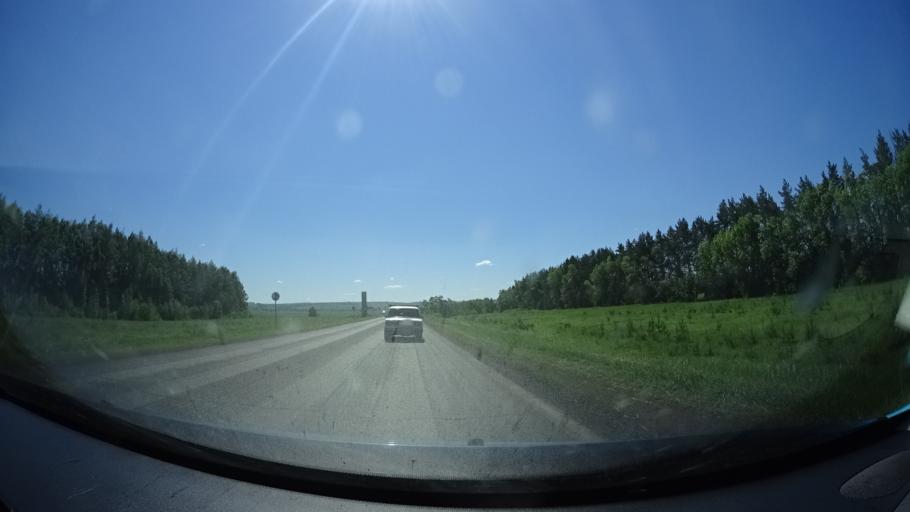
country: RU
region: Bashkortostan
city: Blagoveshchensk
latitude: 55.2264
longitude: 55.7896
